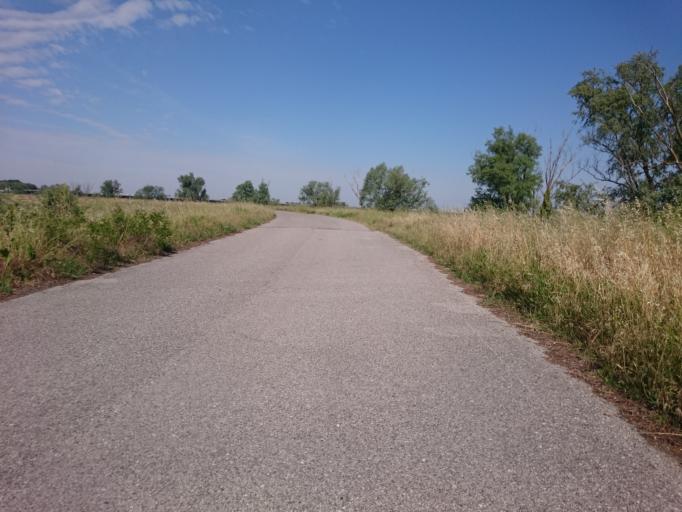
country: IT
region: Veneto
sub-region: Provincia di Rovigo
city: Bottrighe
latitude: 45.0186
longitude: 12.1087
